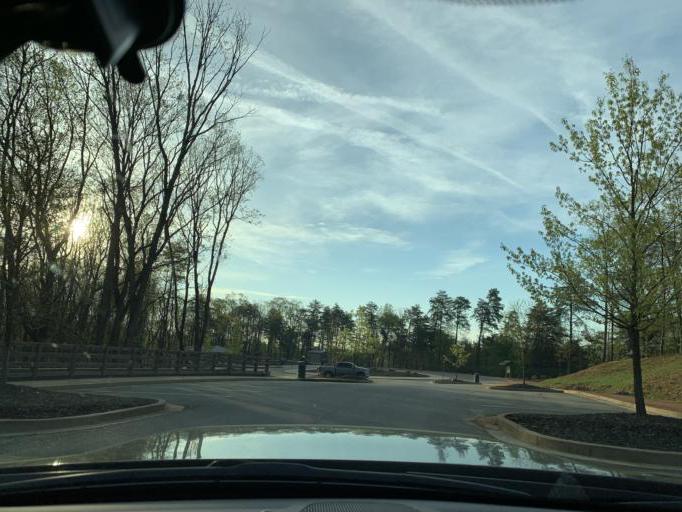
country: US
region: Georgia
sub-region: Forsyth County
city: Cumming
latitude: 34.2434
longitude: -84.1379
